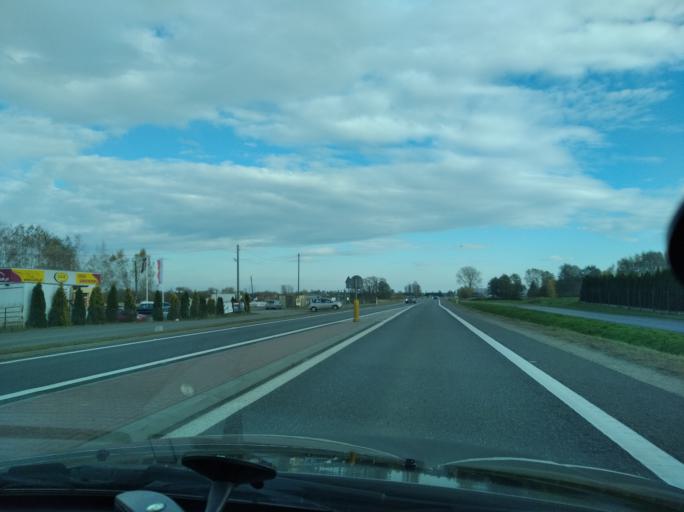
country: PL
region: Subcarpathian Voivodeship
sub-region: Powiat debicki
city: Debica
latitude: 50.0465
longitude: 21.4400
